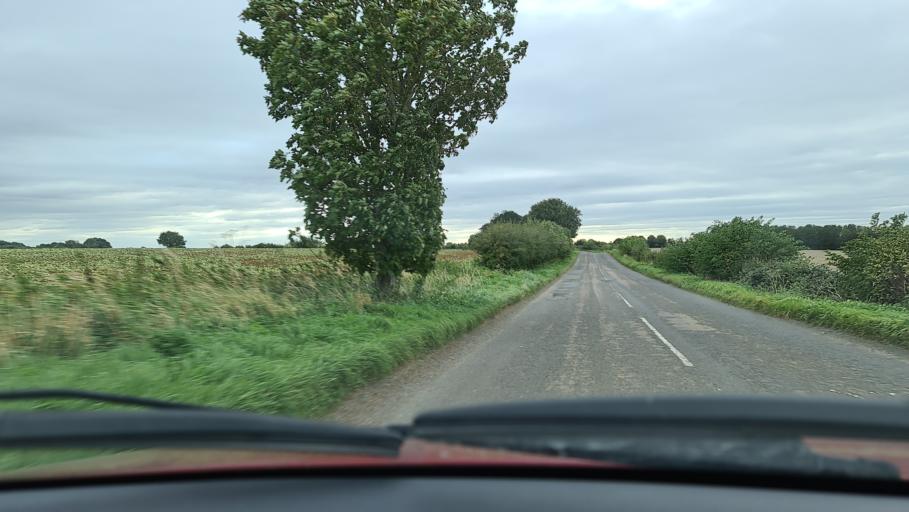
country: GB
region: England
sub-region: Oxfordshire
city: Adderbury
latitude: 52.0136
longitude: -1.2711
